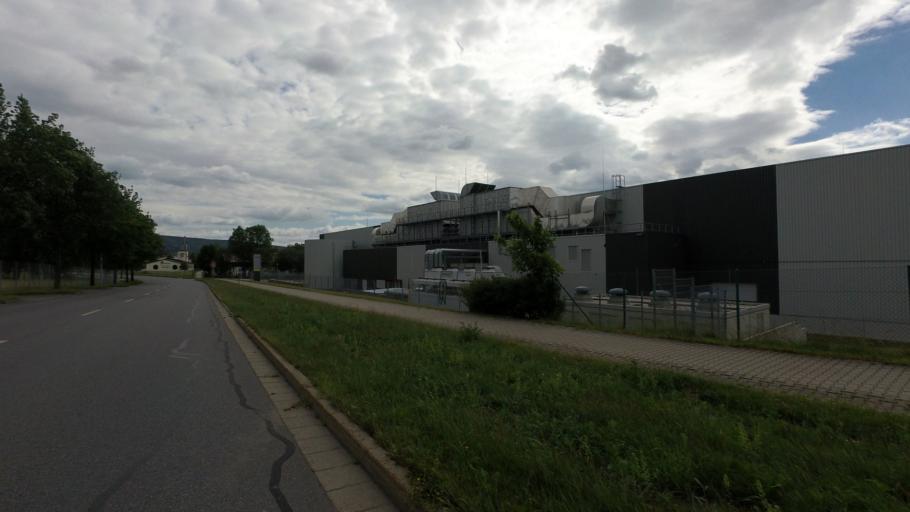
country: DE
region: Saxony
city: Neustadt in Sachsen
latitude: 51.0307
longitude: 14.2298
